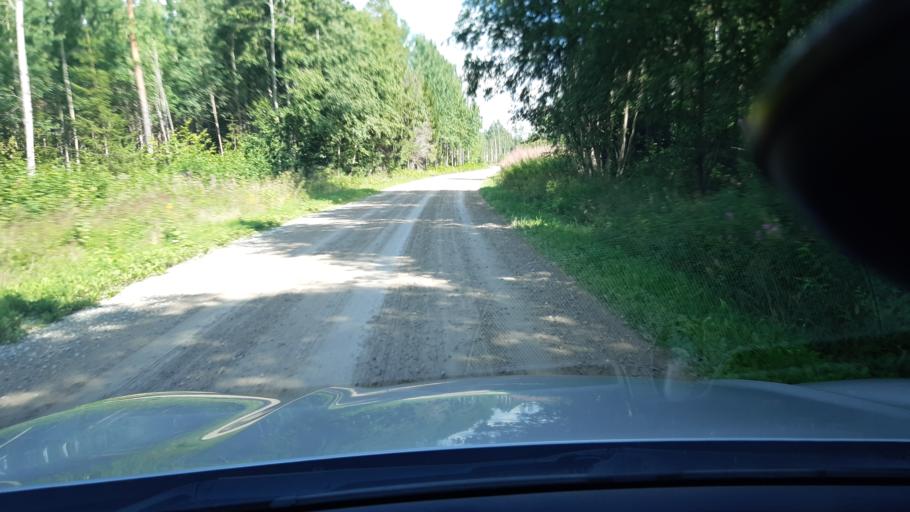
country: EE
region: Jaervamaa
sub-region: Tueri vald
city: Tueri
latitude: 58.9169
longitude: 25.1854
